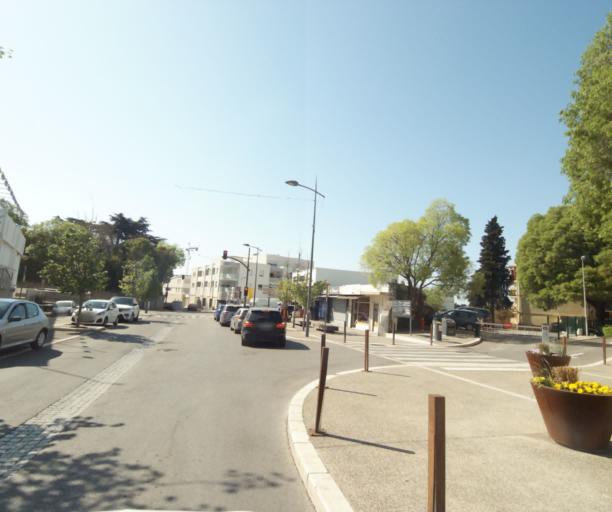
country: FR
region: Languedoc-Roussillon
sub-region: Departement de l'Herault
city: Castelnau-le-Lez
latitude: 43.6324
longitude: 3.8960
